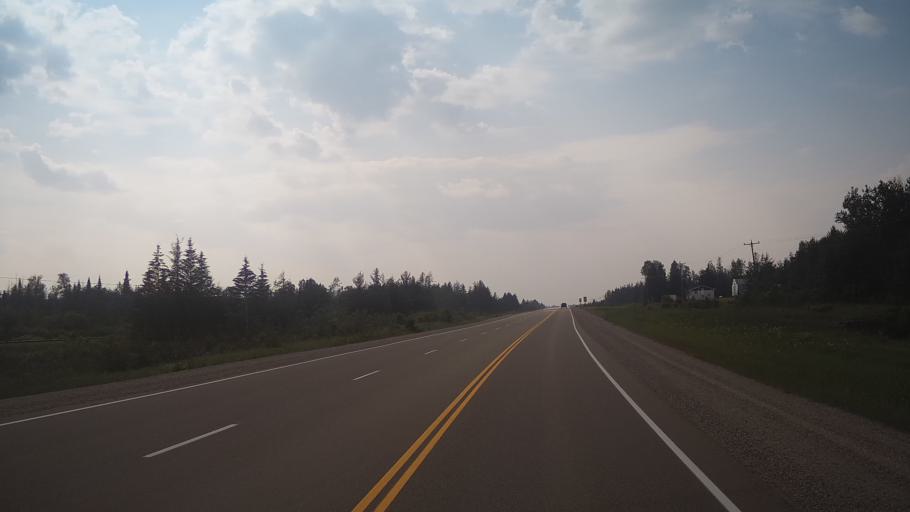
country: CA
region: Ontario
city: Kapuskasing
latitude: 49.4667
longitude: -82.6557
